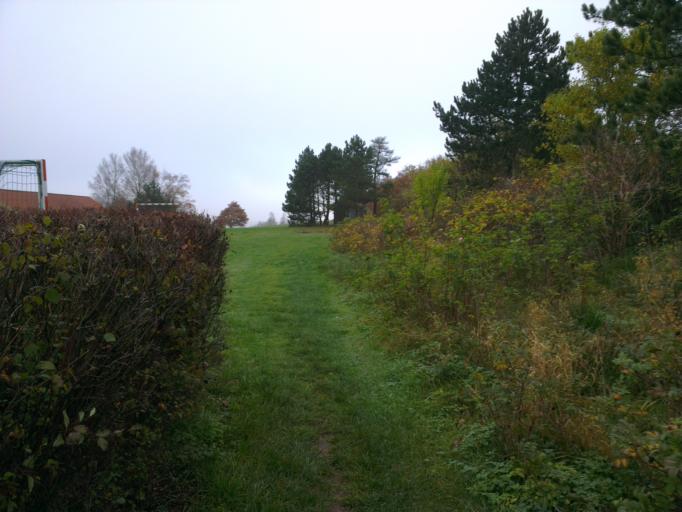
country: DK
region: Capital Region
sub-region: Frederikssund Kommune
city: Jaegerspris
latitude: 55.8493
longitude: 12.0020
